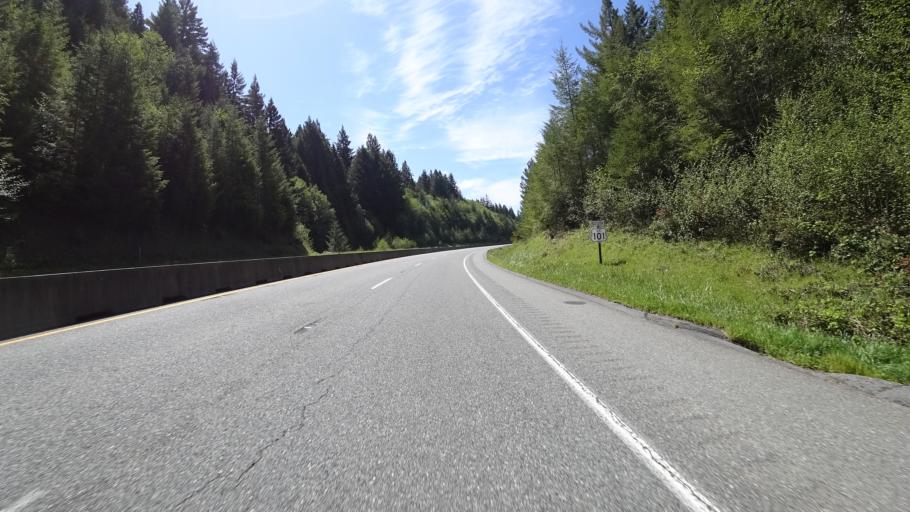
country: US
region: California
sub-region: Humboldt County
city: Westhaven-Moonstone
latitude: 41.3946
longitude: -123.9935
